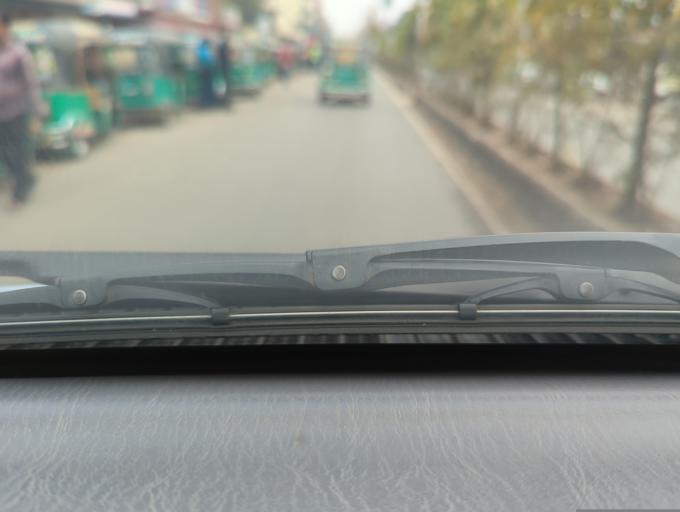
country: BD
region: Sylhet
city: Maulavi Bazar
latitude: 24.4899
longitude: 91.7574
